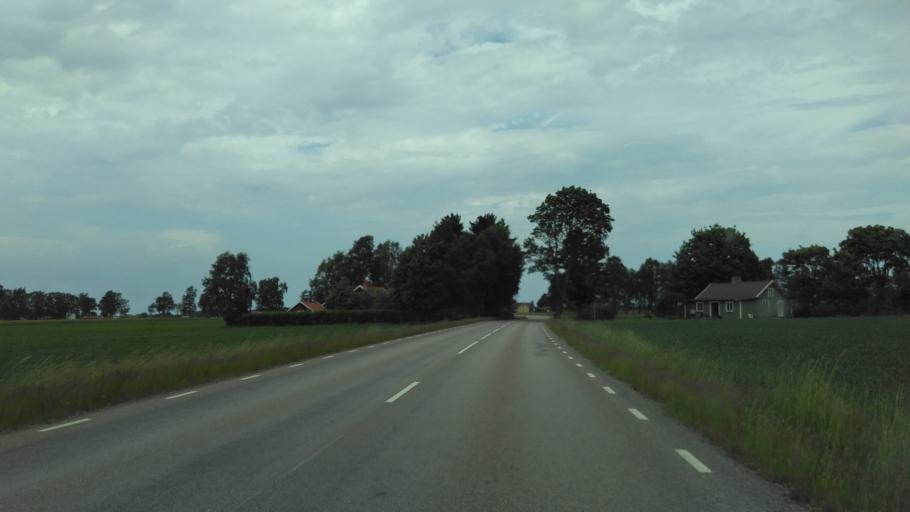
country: SE
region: Vaestra Goetaland
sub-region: Lidkopings Kommun
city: Lidkoping
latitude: 58.4457
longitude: 13.1610
